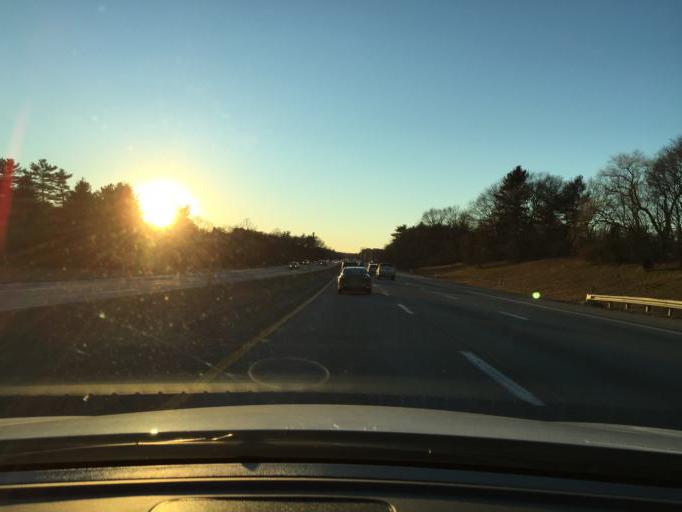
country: US
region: Massachusetts
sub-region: Middlesex County
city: Framingham Center
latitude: 42.3142
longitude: -71.4173
